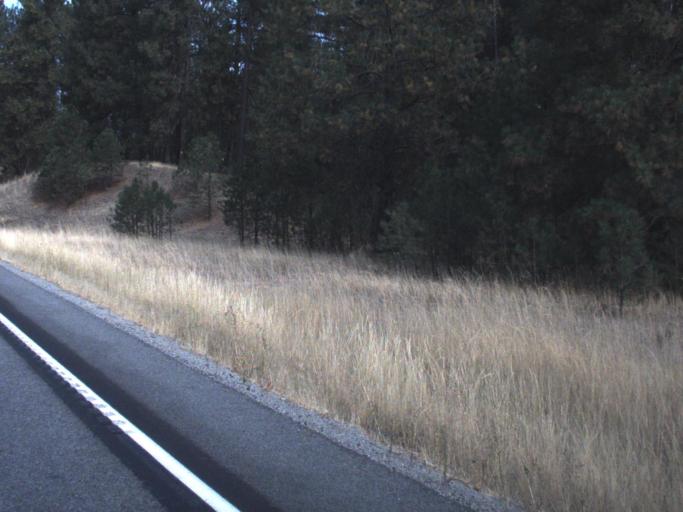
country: US
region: Washington
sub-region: Spokane County
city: Deer Park
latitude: 47.8885
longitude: -117.4254
